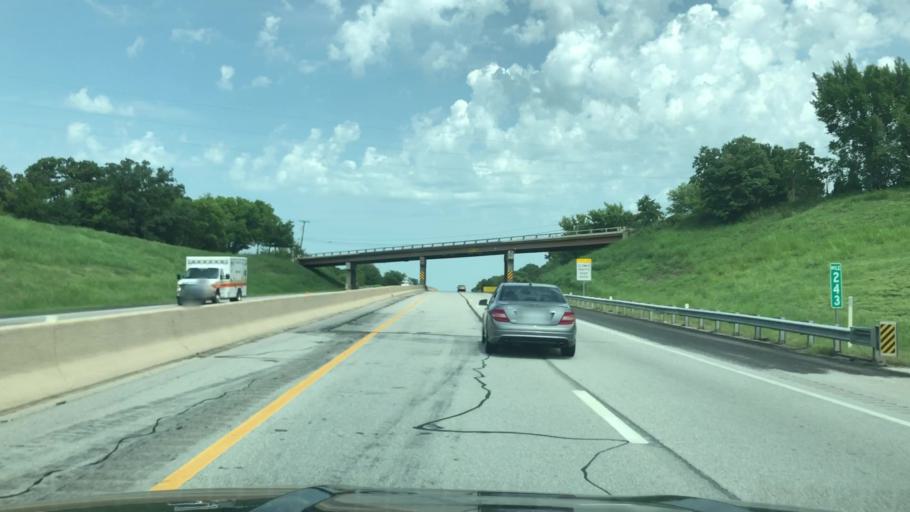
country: US
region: Oklahoma
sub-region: Rogers County
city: Catoosa
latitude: 36.1875
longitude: -95.7275
